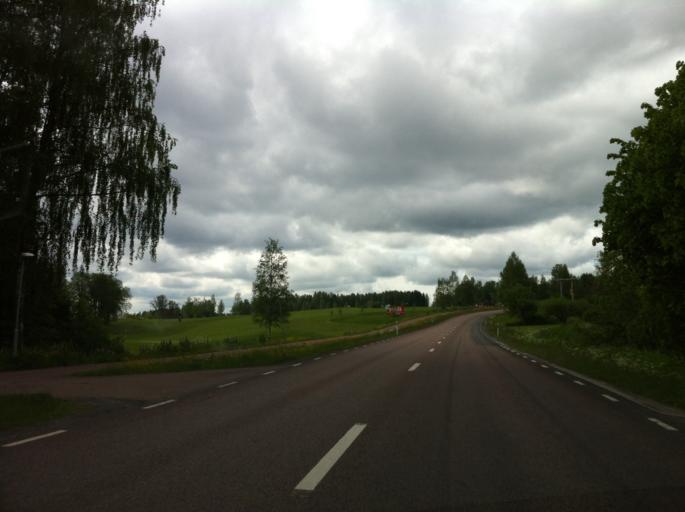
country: SE
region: Vaermland
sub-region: Sunne Kommun
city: Sunne
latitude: 59.8190
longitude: 13.1305
